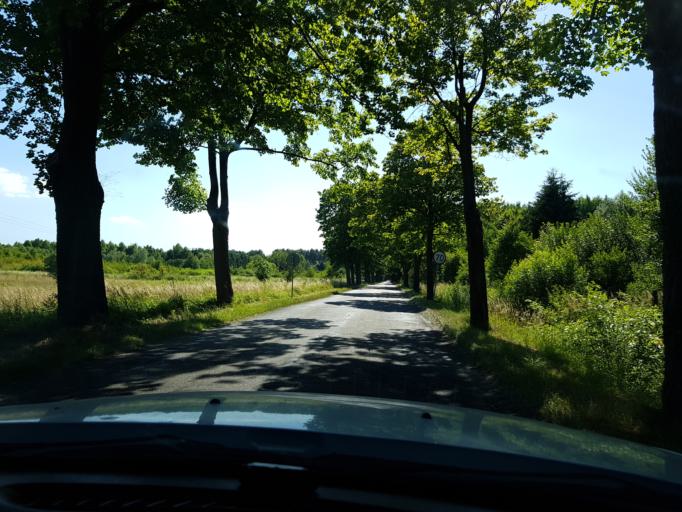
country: PL
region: West Pomeranian Voivodeship
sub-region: Powiat bialogardzki
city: Bialogard
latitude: 53.9975
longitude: 15.9669
